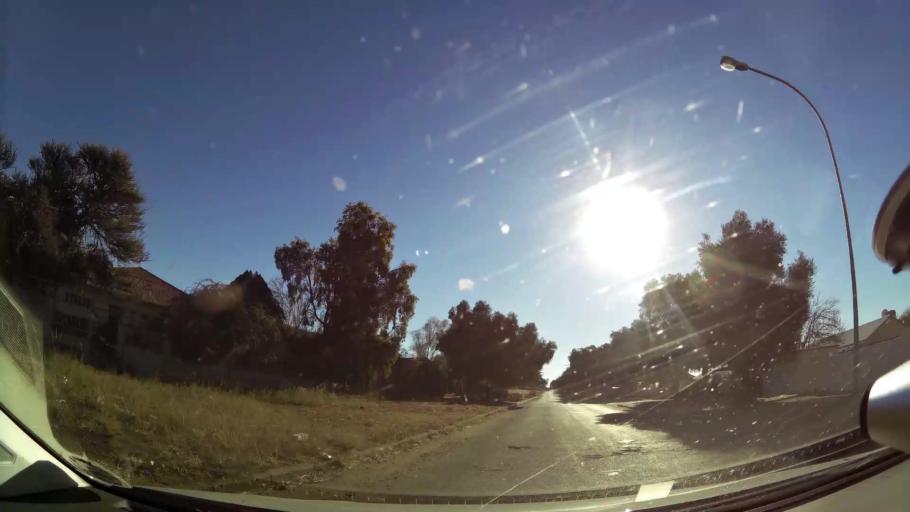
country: ZA
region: Northern Cape
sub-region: Frances Baard District Municipality
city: Kimberley
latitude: -28.7576
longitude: 24.7757
